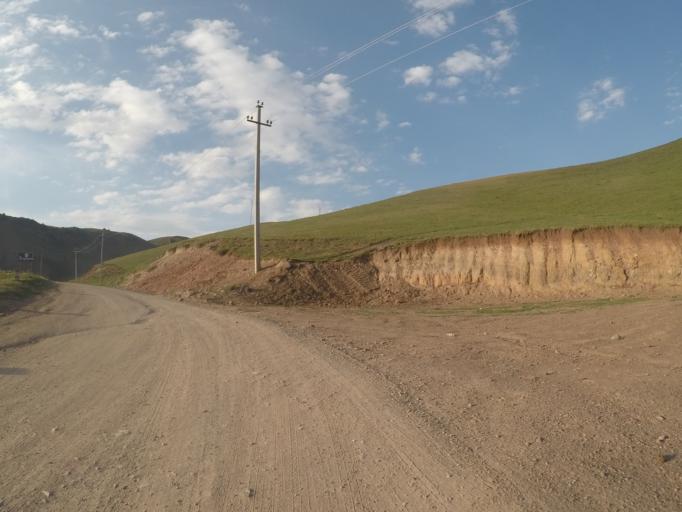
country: KG
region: Chuy
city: Bishkek
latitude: 42.6406
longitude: 74.6285
